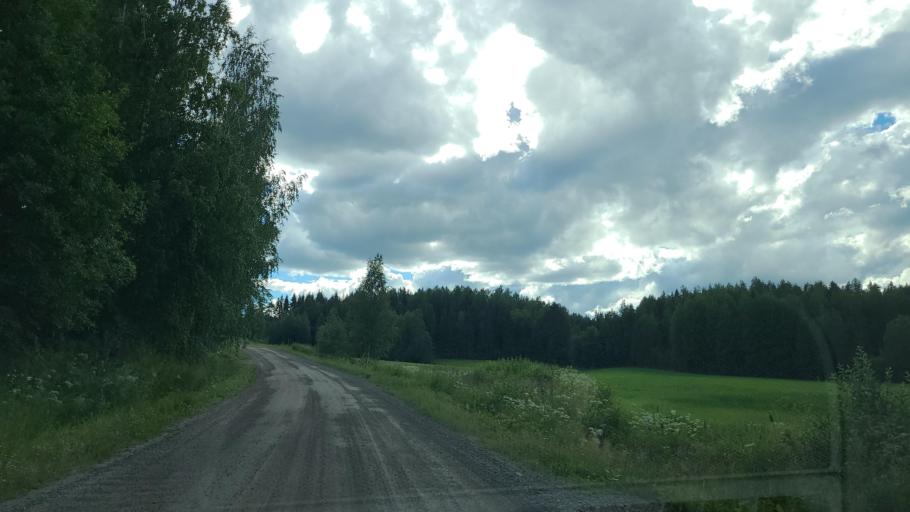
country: FI
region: Central Finland
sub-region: Jaemsae
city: Jaemsae
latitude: 61.9341
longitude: 25.3322
